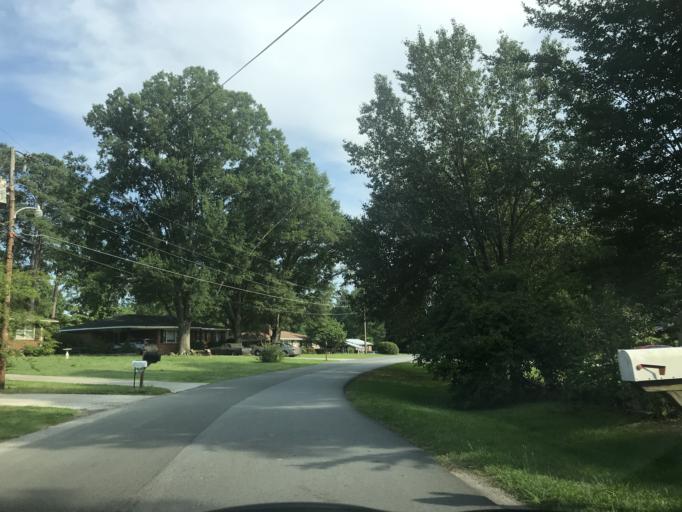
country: US
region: North Carolina
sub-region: Wake County
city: Raleigh
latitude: 35.8191
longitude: -78.5716
